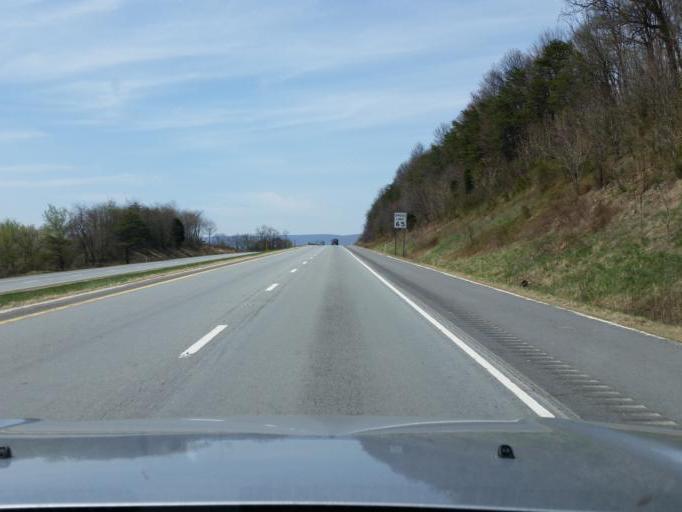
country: US
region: Pennsylvania
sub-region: Perry County
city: Newport
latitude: 40.4964
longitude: -77.1182
